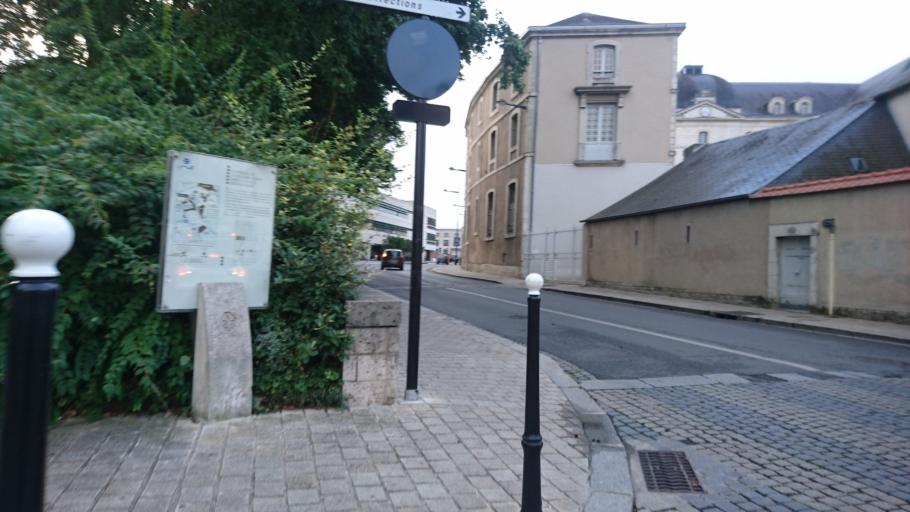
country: FR
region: Centre
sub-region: Departement du Cher
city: Bourges
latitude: 47.0812
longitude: 2.3980
